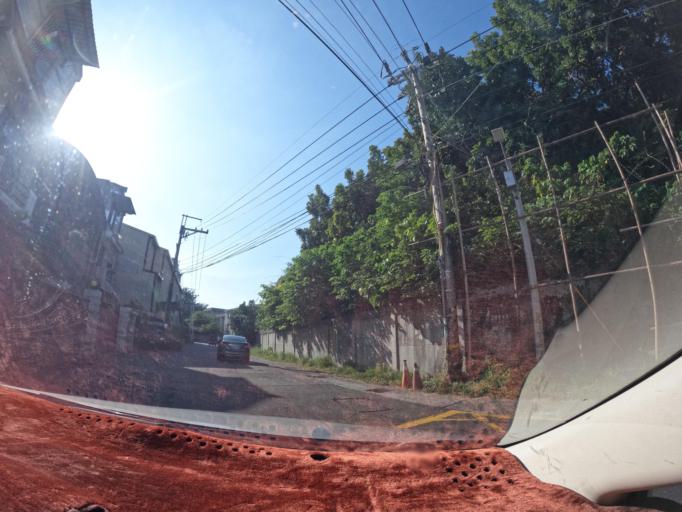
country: TW
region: Taiwan
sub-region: Tainan
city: Tainan
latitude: 23.0239
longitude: 120.2454
